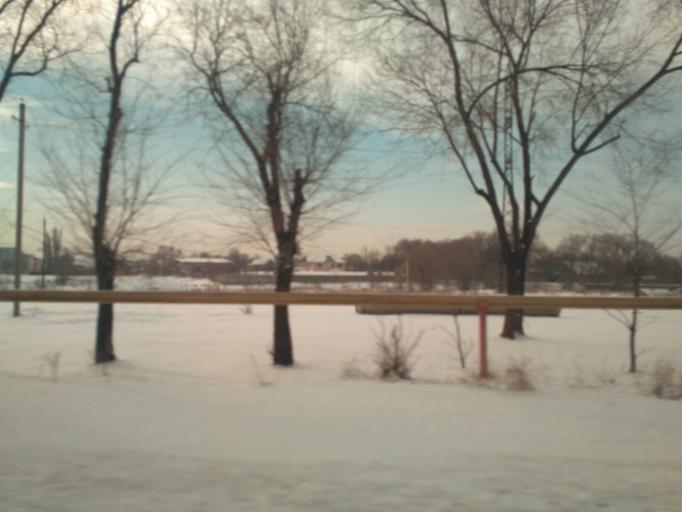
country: KZ
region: Almaty Qalasy
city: Almaty
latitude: 43.2156
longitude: 76.7720
